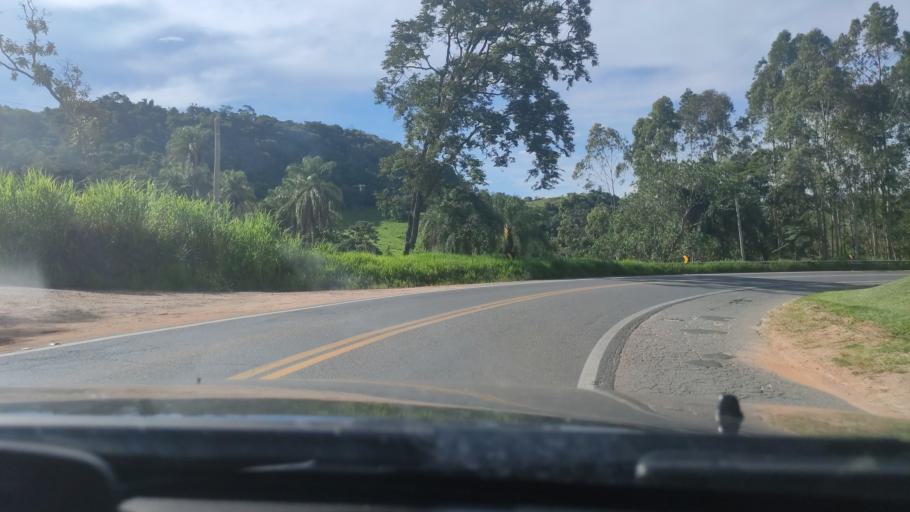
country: BR
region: Sao Paulo
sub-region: Aguas De Lindoia
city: Aguas de Lindoia
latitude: -22.5352
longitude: -46.6349
